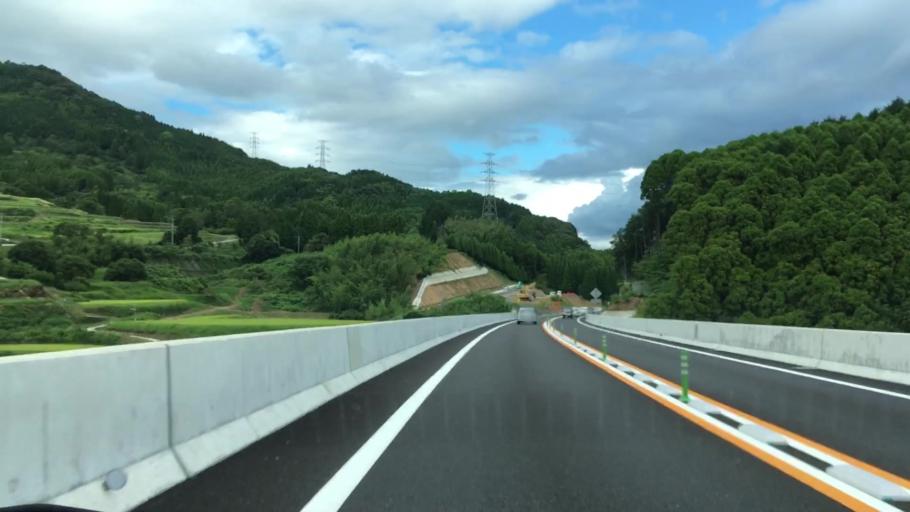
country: JP
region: Saga Prefecture
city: Imaricho-ko
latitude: 33.3118
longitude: 129.9177
